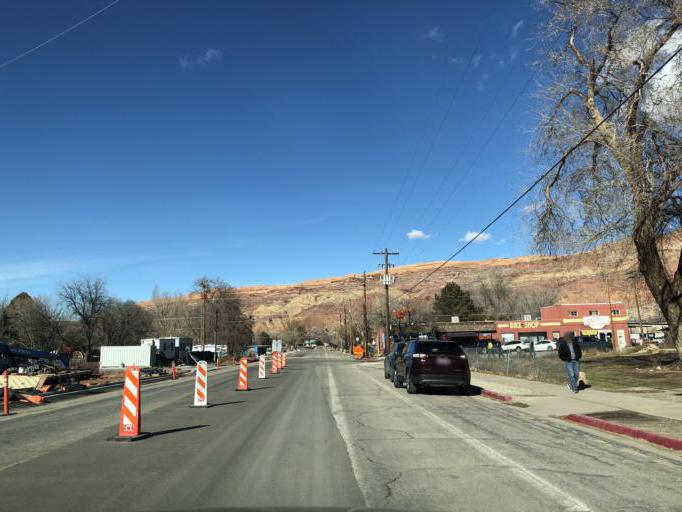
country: US
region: Utah
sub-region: Grand County
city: Moab
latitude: 38.5742
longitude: -109.5527
